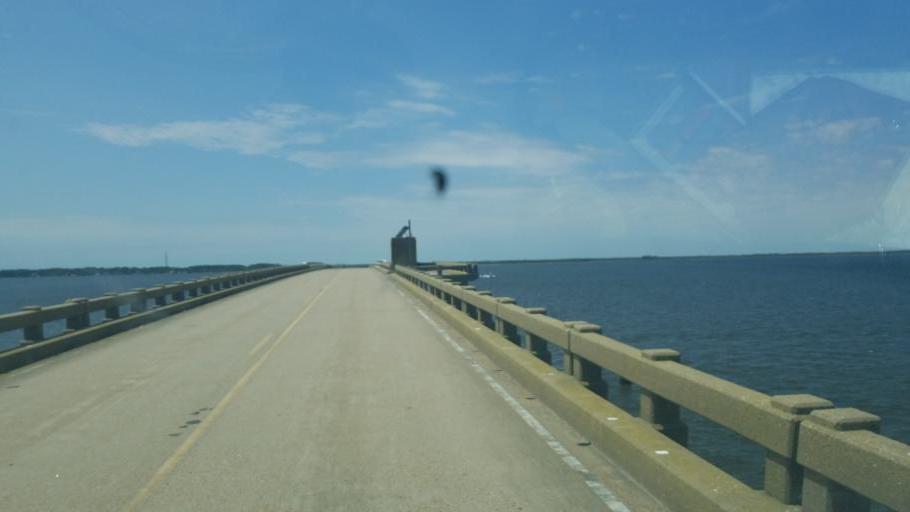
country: US
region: North Carolina
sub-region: Dare County
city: Manteo
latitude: 35.9194
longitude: -75.7469
